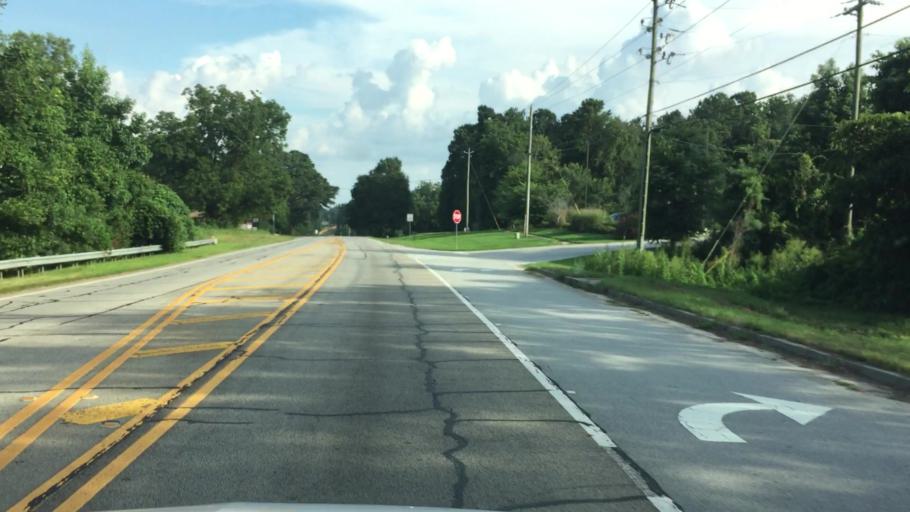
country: US
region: Georgia
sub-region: Henry County
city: Stockbridge
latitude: 33.5828
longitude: -84.1493
